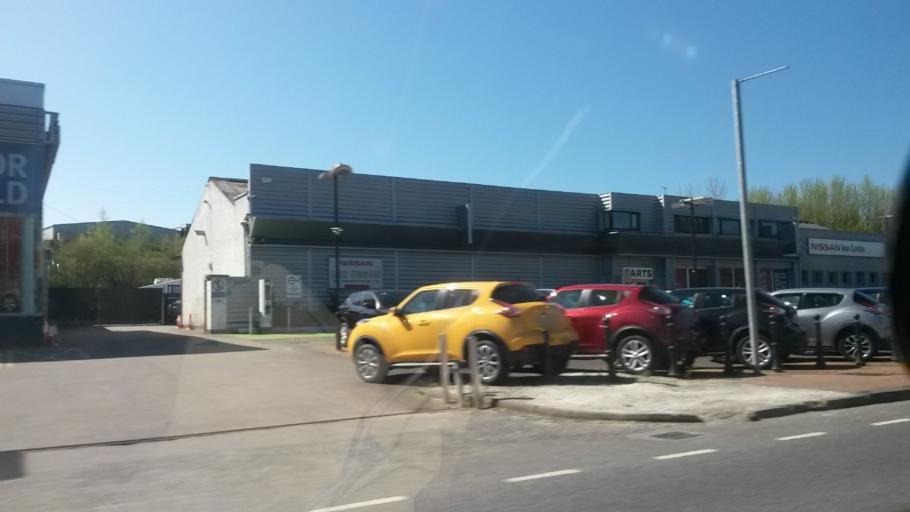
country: IE
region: Munster
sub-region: County Cork
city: Cork
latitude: 51.8937
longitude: -8.5146
